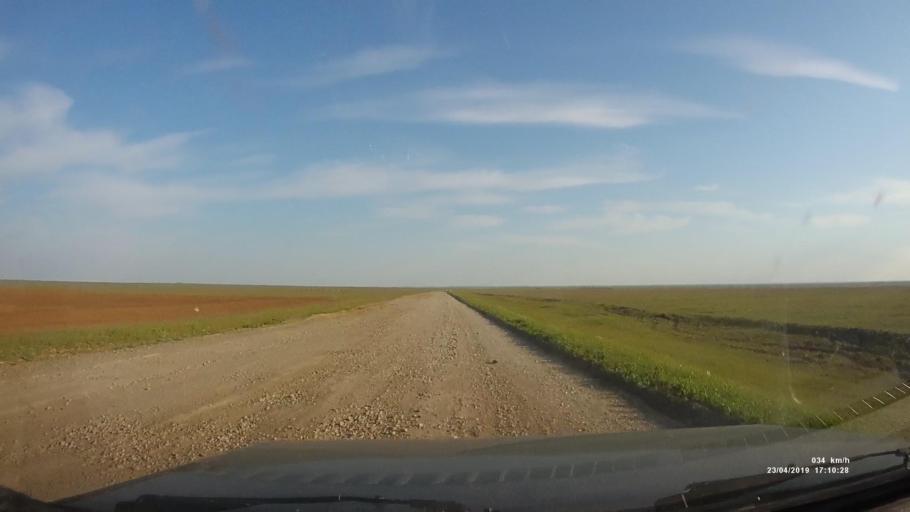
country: RU
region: Kalmykiya
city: Priyutnoye
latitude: 46.2465
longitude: 43.4842
